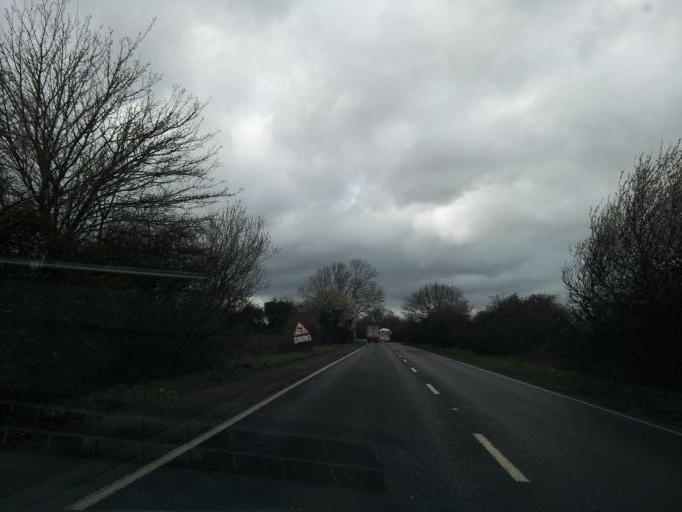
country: GB
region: England
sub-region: Somerset
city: Stoke-sub-Hamdon
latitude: 50.9641
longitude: -2.7319
